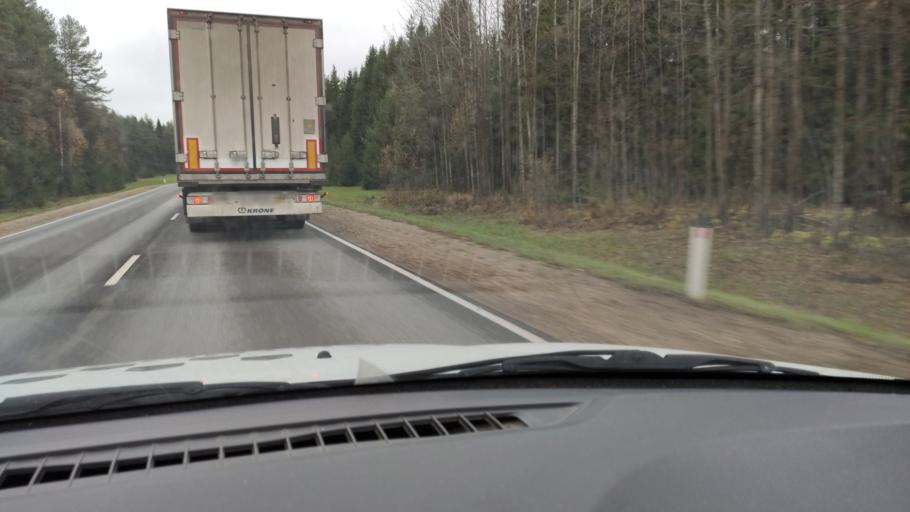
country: RU
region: Kirov
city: Slobodskoy
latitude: 58.7688
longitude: 50.3667
